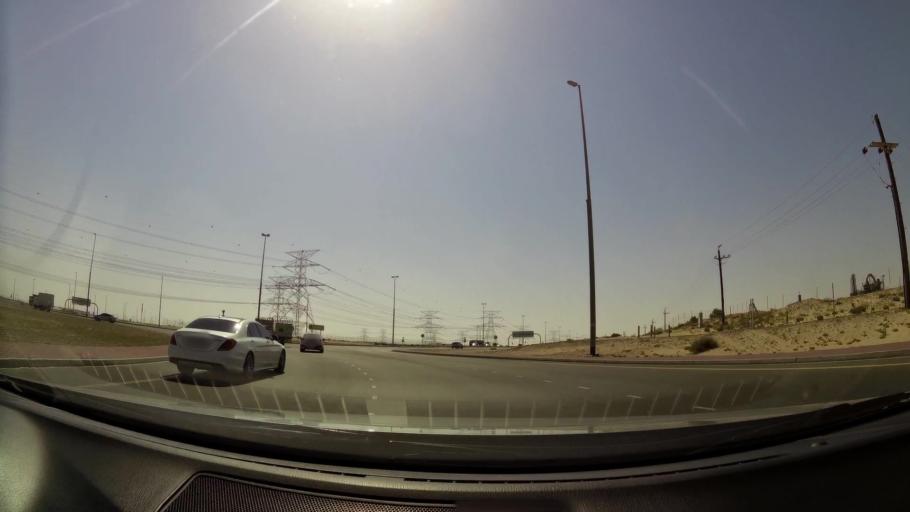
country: AE
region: Dubai
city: Dubai
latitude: 24.9363
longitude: 55.0761
